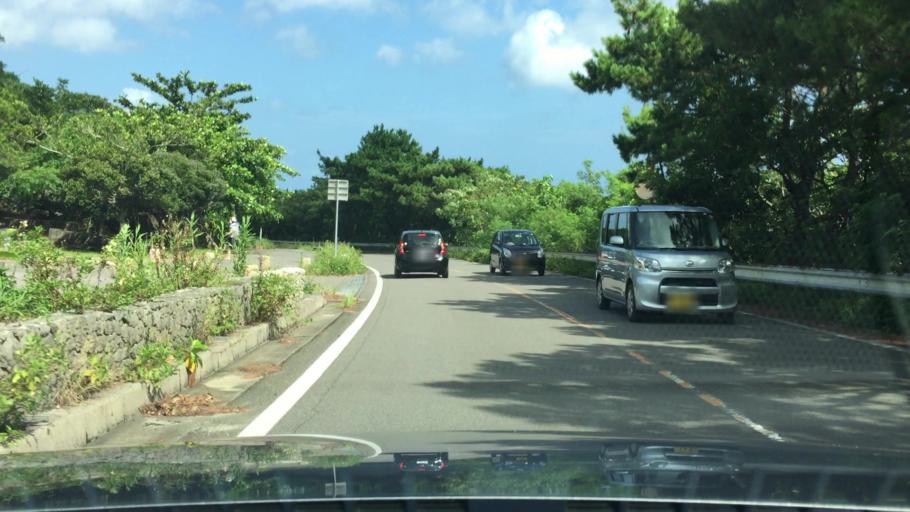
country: JP
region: Okinawa
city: Ishigaki
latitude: 24.4493
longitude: 124.2101
